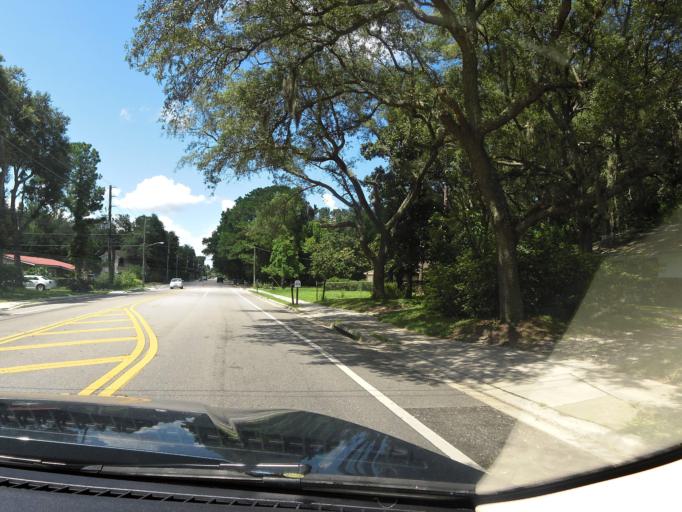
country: US
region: Florida
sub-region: Nassau County
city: Fernandina Beach
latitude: 30.6615
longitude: -81.4527
